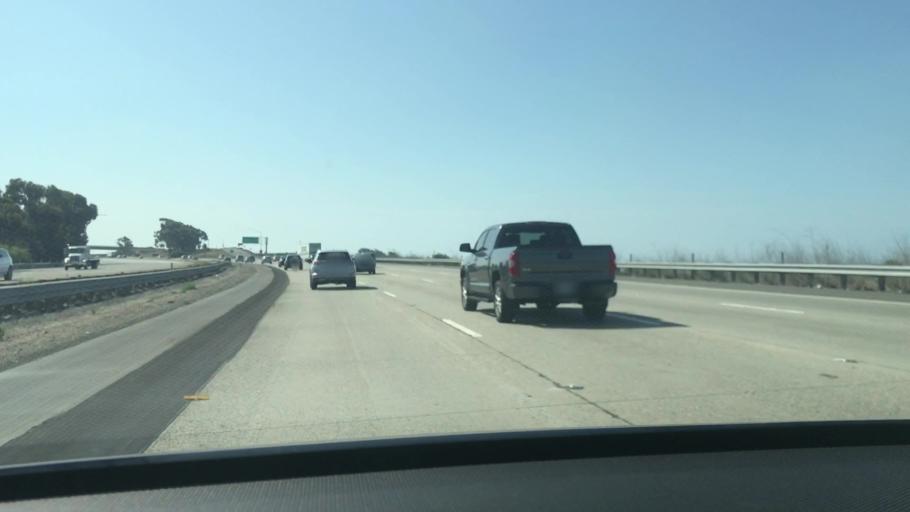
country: US
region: California
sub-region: Orange County
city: San Clemente
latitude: 33.3890
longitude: -117.5884
